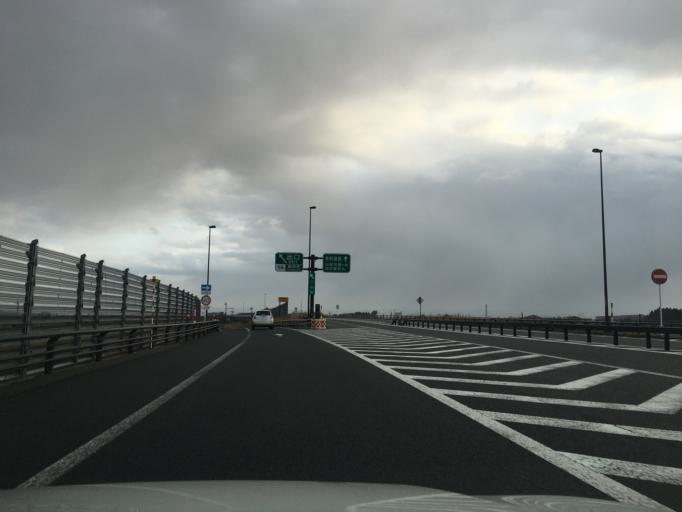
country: JP
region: Yamagata
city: Tsuruoka
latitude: 38.7149
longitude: 139.7561
